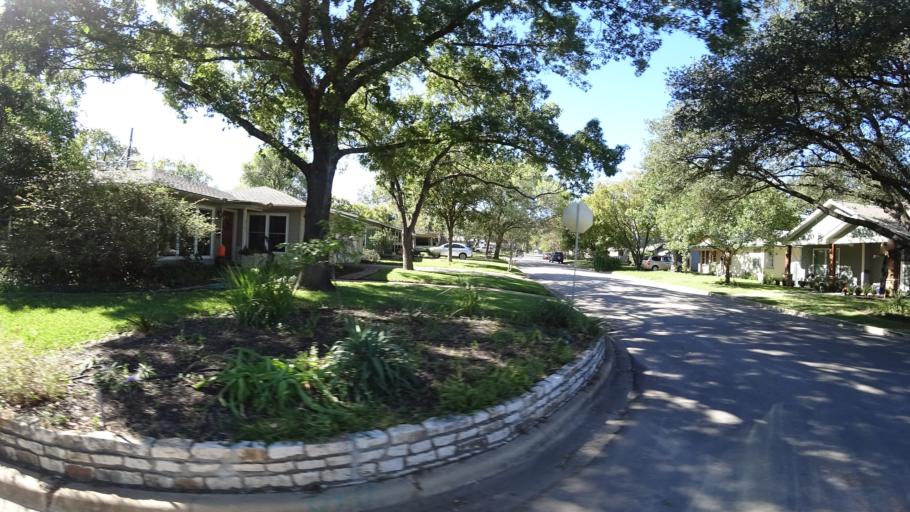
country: US
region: Texas
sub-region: Travis County
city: Austin
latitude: 30.3250
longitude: -97.7491
